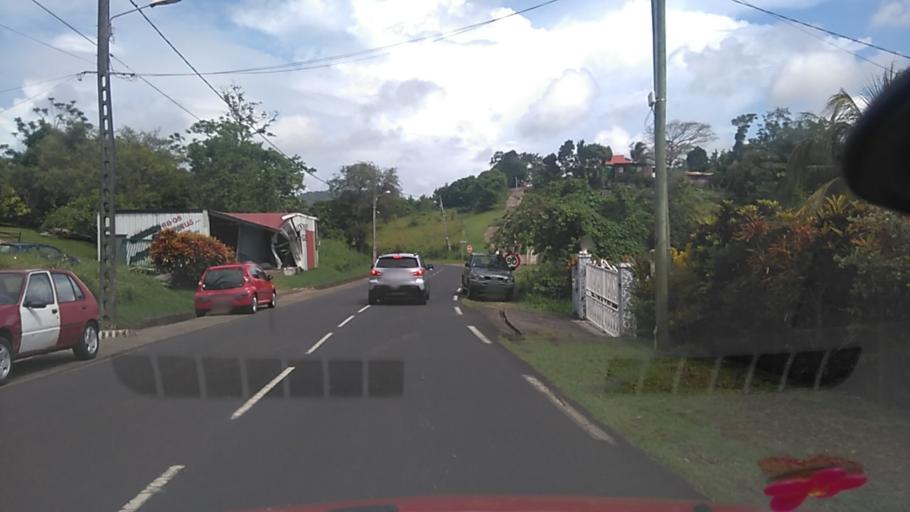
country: MQ
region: Martinique
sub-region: Martinique
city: Le Francois
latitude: 14.5977
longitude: -60.9290
